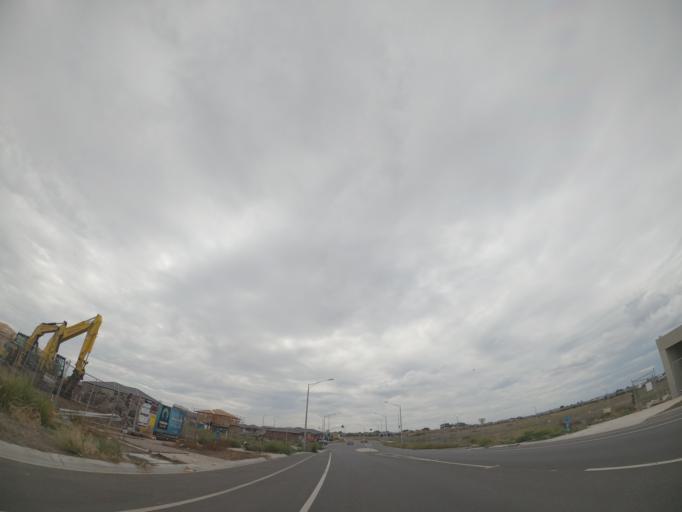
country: AU
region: Victoria
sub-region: Hume
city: Roxburgh Park
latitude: -37.5749
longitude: 144.8968
